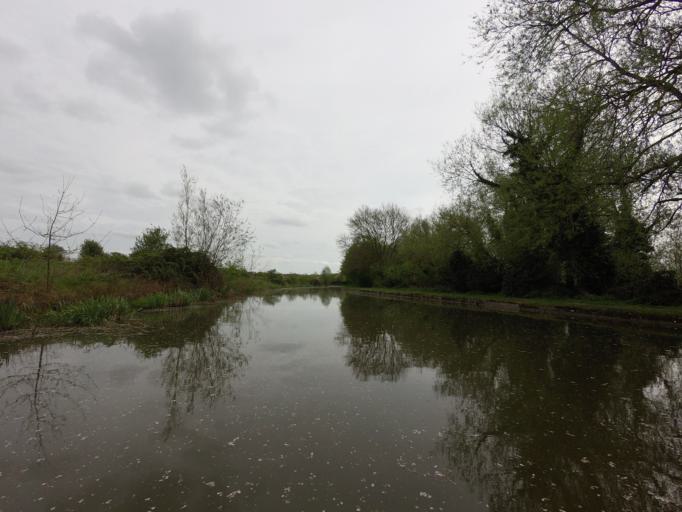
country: GB
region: England
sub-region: Milton Keynes
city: Bradwell
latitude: 52.0732
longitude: -0.7820
